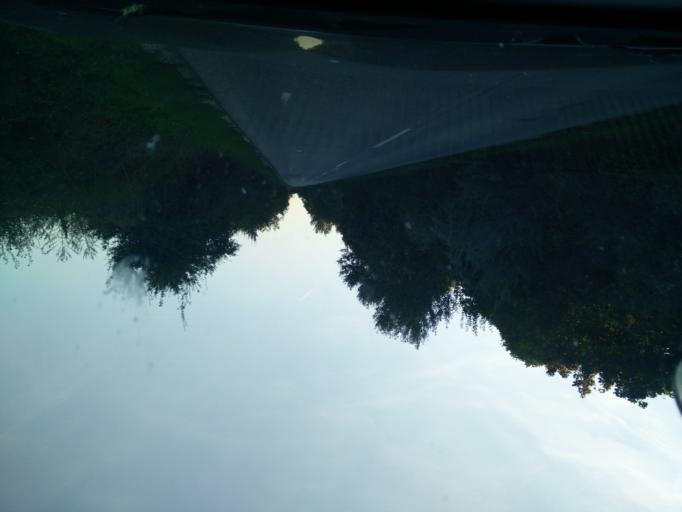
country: HU
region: Pest
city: Perbal
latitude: 47.6099
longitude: 18.7703
